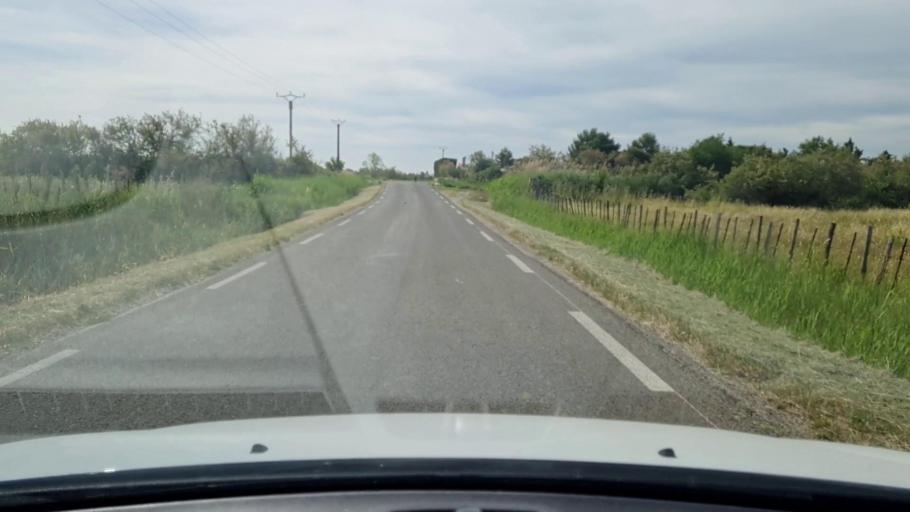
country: FR
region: Languedoc-Roussillon
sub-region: Departement du Gard
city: Aigues-Mortes
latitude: 43.6129
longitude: 4.2085
